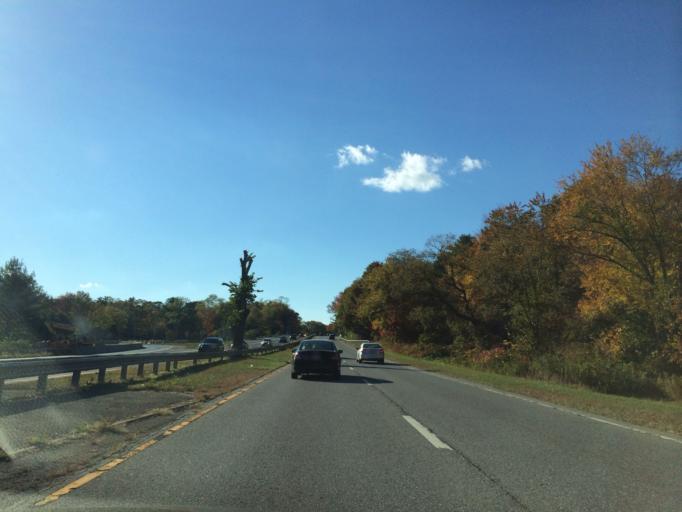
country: US
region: Connecticut
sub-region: Fairfield County
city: Westport
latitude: 41.1637
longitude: -73.3717
